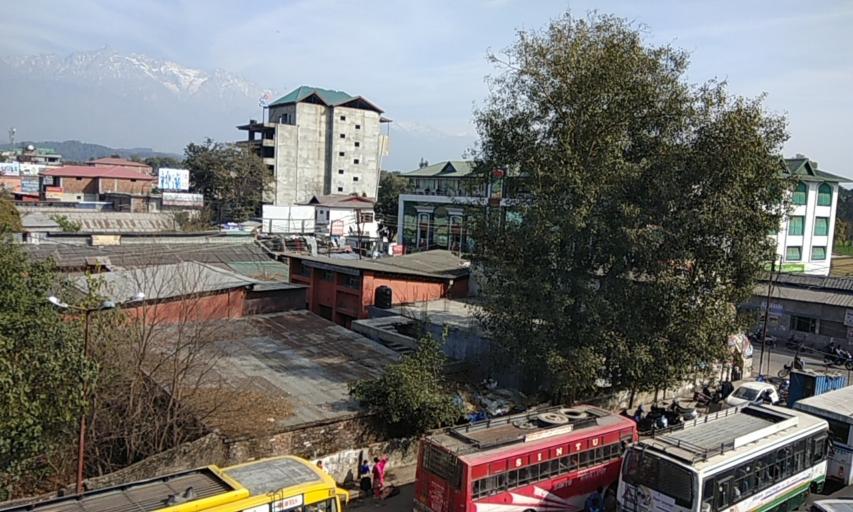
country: IN
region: Himachal Pradesh
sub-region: Kangra
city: Kangra
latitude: 32.1111
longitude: 76.2782
